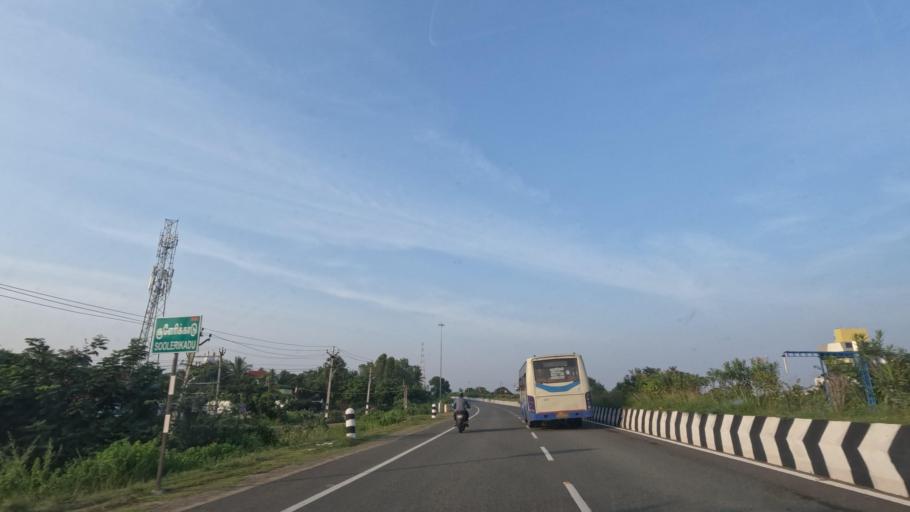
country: IN
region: Tamil Nadu
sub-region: Kancheepuram
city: Mamallapuram
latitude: 12.7036
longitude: 80.2231
